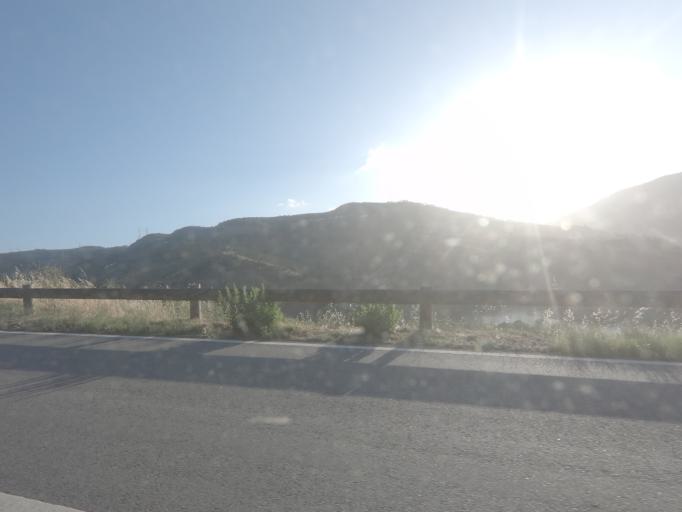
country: PT
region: Viseu
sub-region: Armamar
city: Armamar
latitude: 41.1543
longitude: -7.6374
